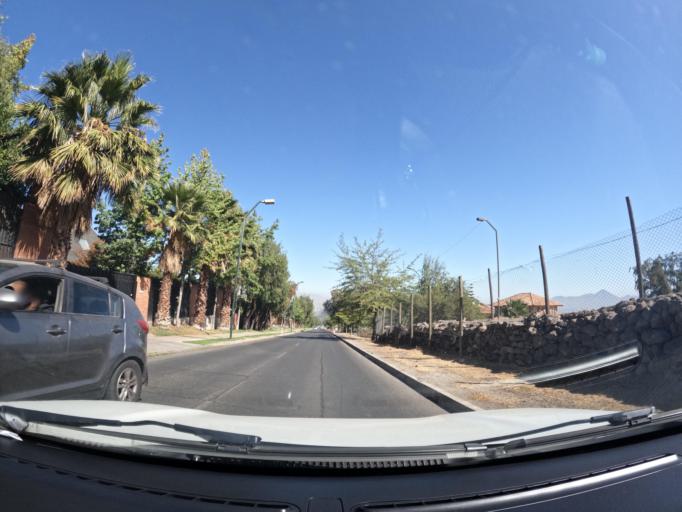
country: CL
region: Santiago Metropolitan
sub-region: Provincia de Santiago
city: Villa Presidente Frei, Nunoa, Santiago, Chile
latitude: -33.4978
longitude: -70.5213
